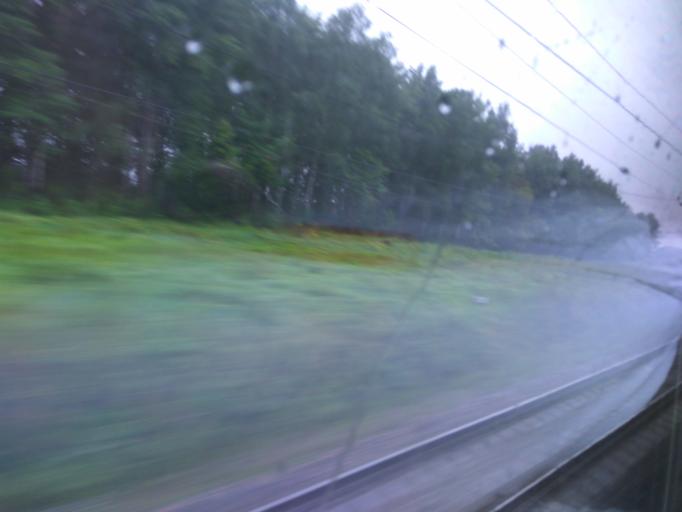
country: RU
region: Moskovskaya
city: Ozherel'ye
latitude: 54.8436
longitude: 38.2310
